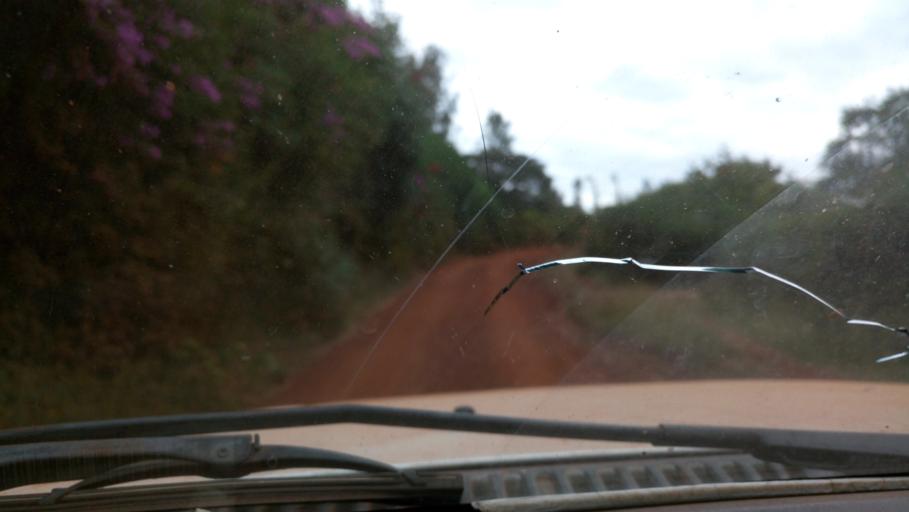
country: KE
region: Murang'a District
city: Karuri
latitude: -0.7069
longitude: 37.2005
